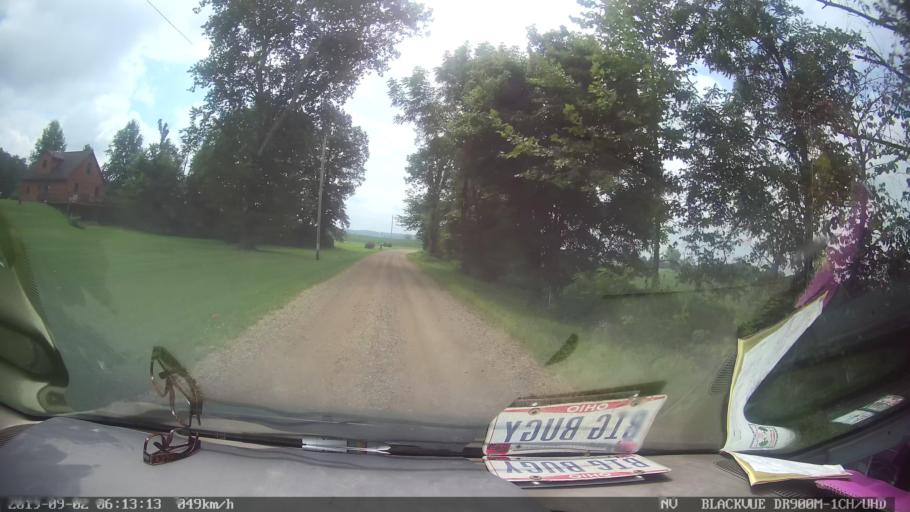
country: US
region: Ohio
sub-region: Knox County
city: Fredericktown
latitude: 40.4775
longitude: -82.6560
